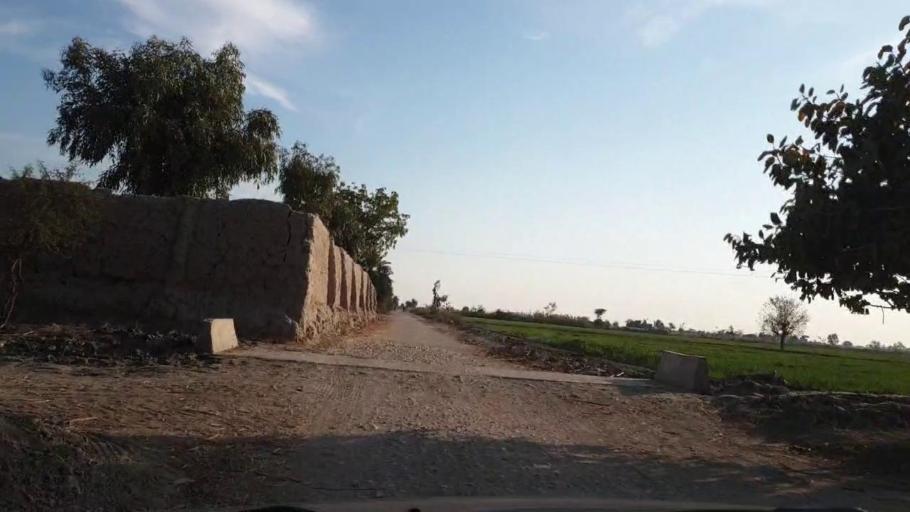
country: PK
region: Sindh
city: Khadro
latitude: 26.1713
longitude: 68.7529
